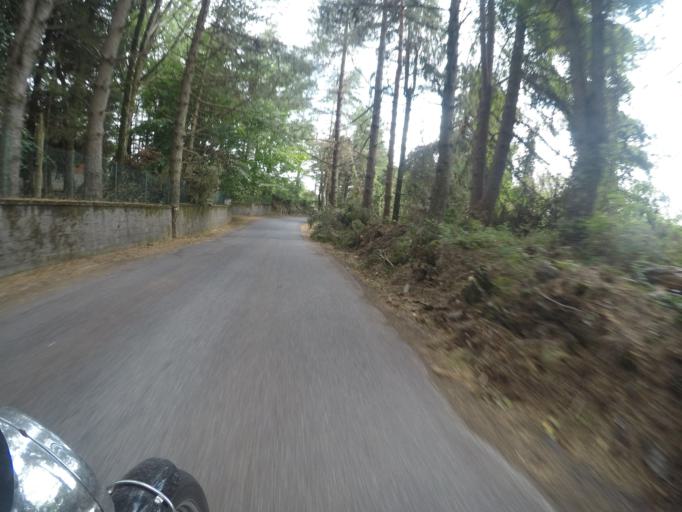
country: IT
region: Tuscany
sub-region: Provincia di Massa-Carrara
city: Carrara
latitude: 44.1172
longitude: 10.1033
